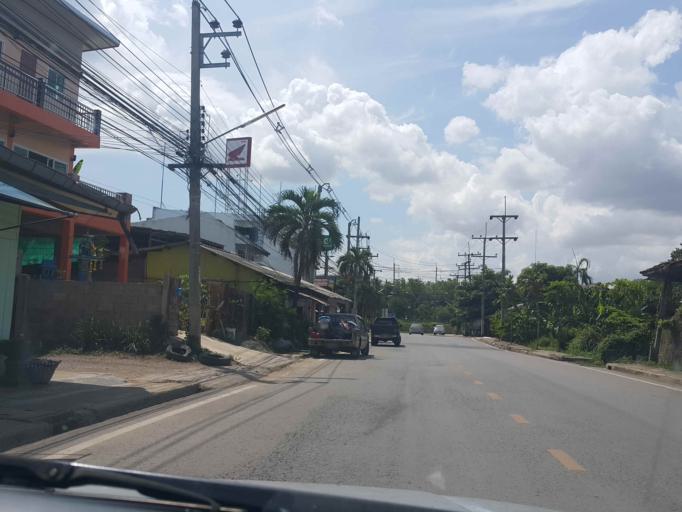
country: TH
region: Phayao
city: Phayao
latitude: 19.1640
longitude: 99.9113
